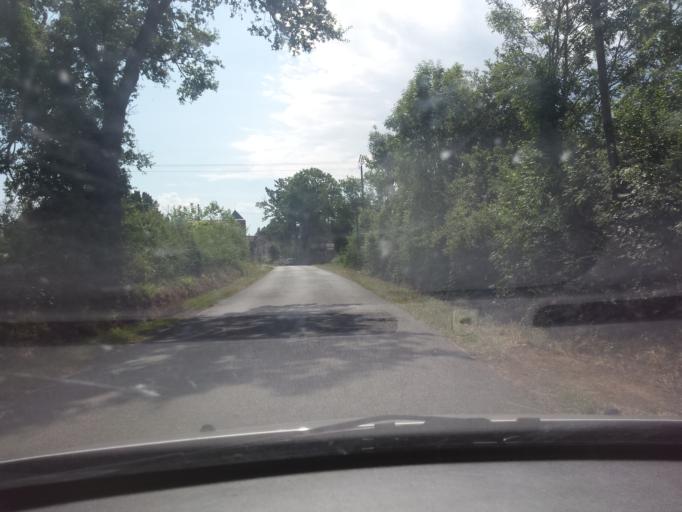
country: FR
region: Poitou-Charentes
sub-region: Departement de la Vienne
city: Availles-Limouzine
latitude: 46.1045
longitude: 0.6991
